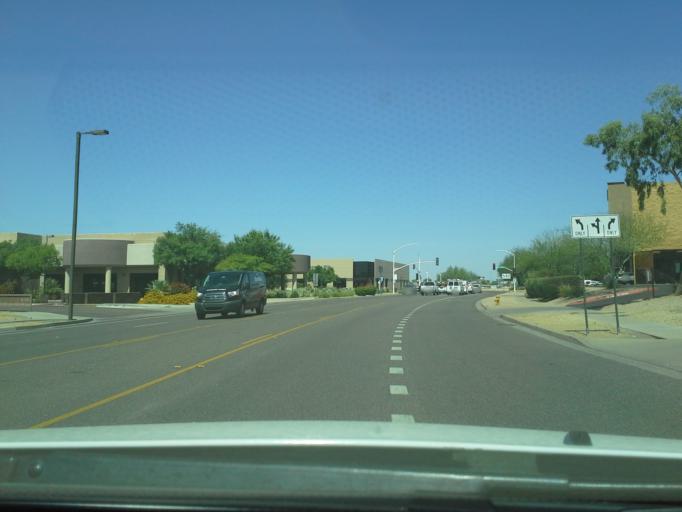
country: US
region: Arizona
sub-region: Maricopa County
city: Paradise Valley
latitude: 33.6192
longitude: -111.9061
